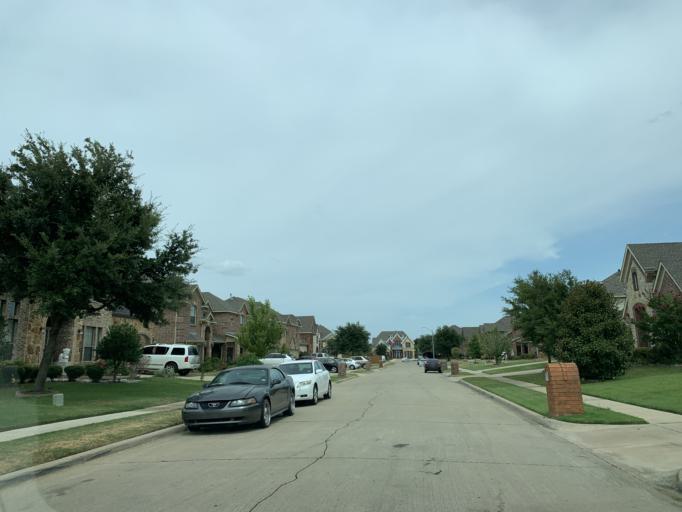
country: US
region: Texas
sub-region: Dallas County
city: Grand Prairie
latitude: 32.6555
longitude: -97.0383
